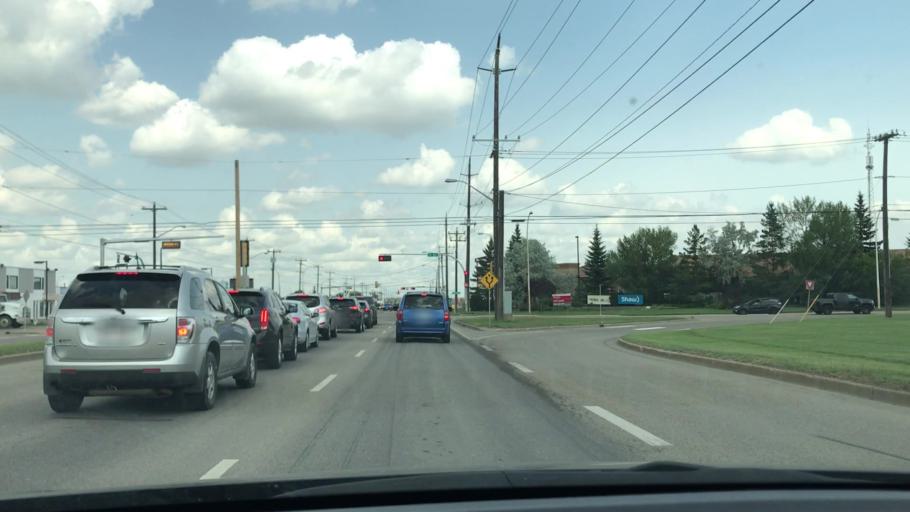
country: CA
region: Alberta
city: Edmonton
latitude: 53.5118
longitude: -113.4183
